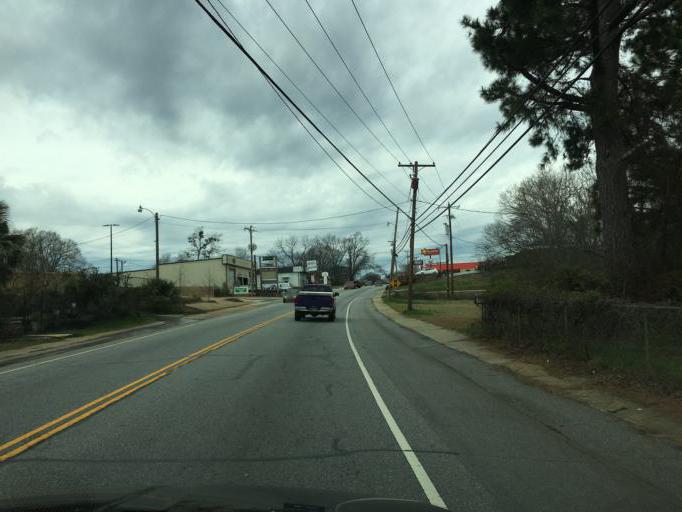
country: US
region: South Carolina
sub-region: Anderson County
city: Piedmont
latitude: 34.7004
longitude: -82.4737
